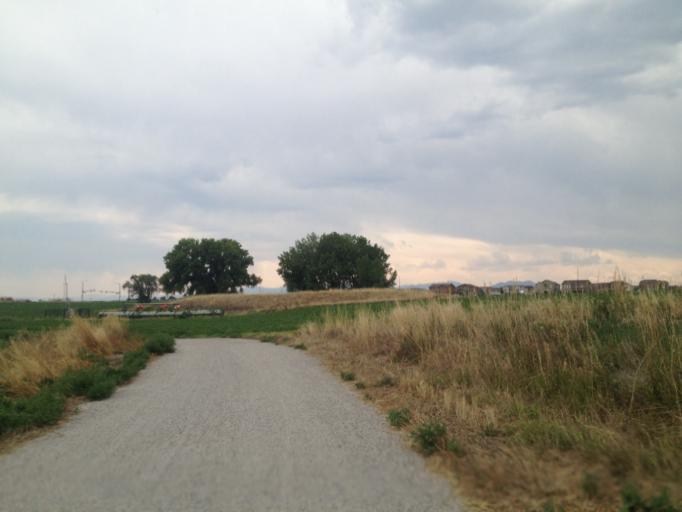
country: US
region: Colorado
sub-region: Boulder County
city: Erie
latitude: 40.0180
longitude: -105.0522
